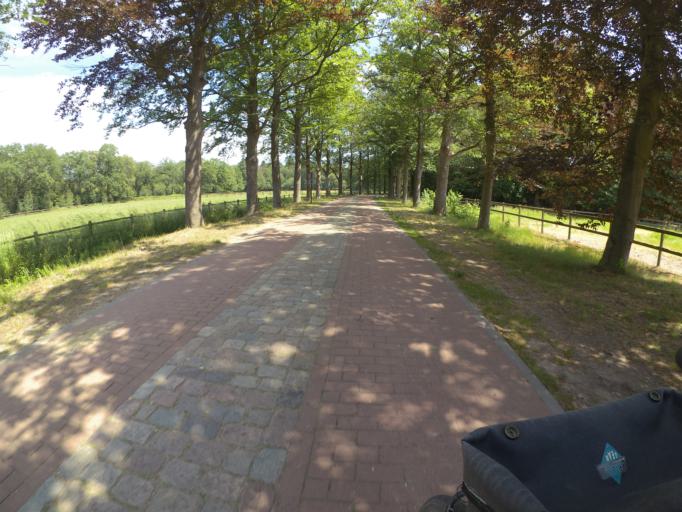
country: NL
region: North Brabant
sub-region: Gemeente Oirschot
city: Oostelbeers
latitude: 51.4878
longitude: 5.2554
